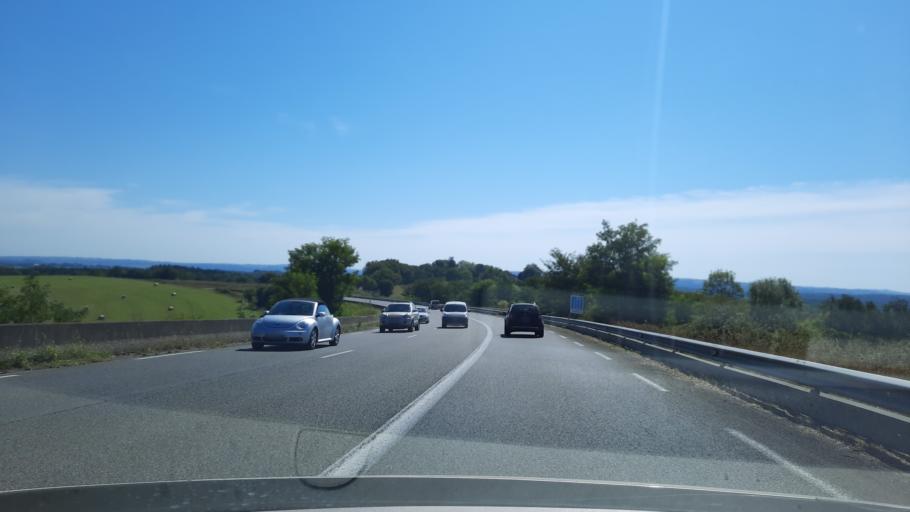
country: FR
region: Midi-Pyrenees
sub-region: Departement de l'Aveyron
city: Villefranche-de-Rouergue
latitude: 44.3315
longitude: 1.9291
